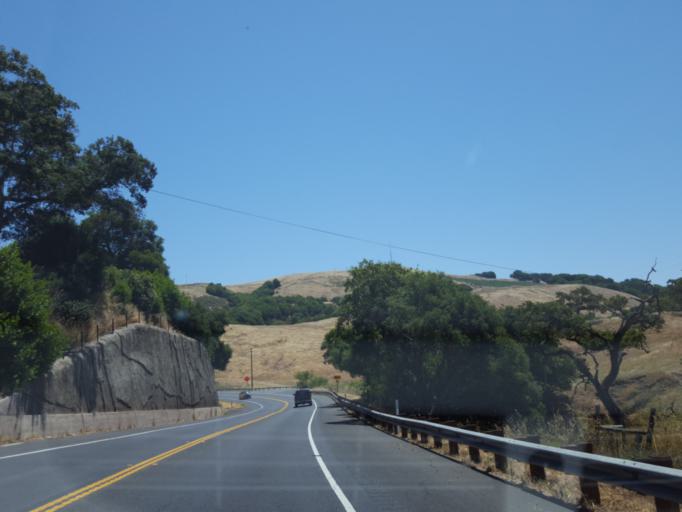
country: US
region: California
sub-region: Sonoma County
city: Temelec
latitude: 38.2367
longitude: -122.5116
